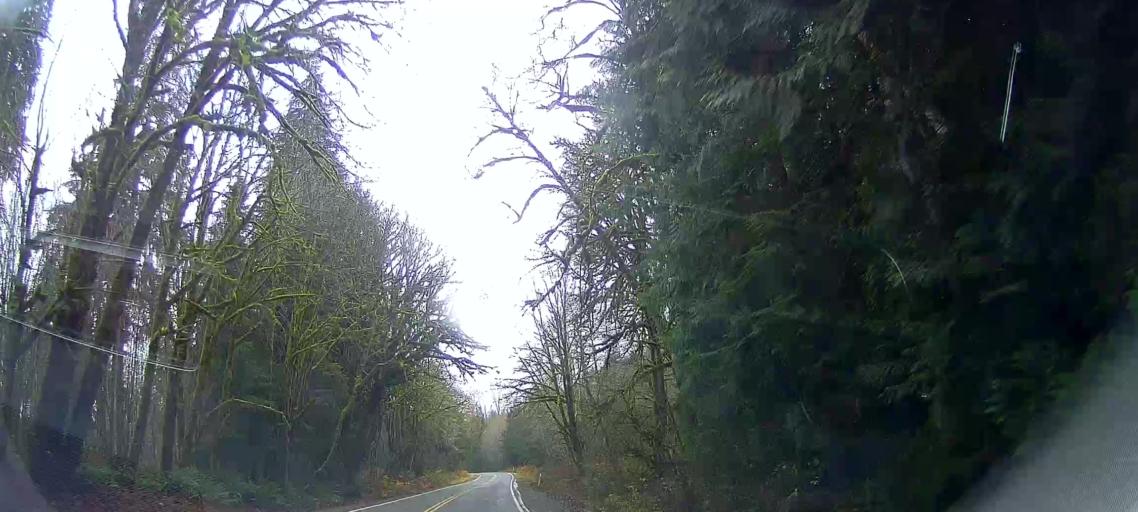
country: US
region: Washington
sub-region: Skagit County
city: Sedro-Woolley
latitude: 48.5112
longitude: -121.9239
